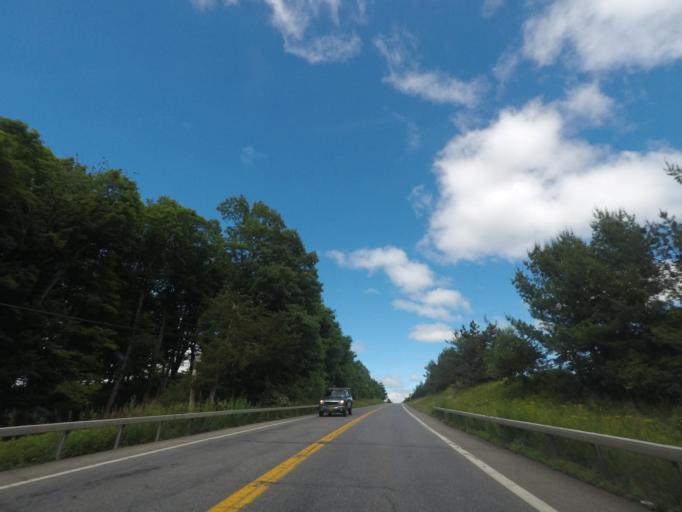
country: US
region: New York
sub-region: Columbia County
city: Philmont
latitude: 42.2081
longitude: -73.6636
